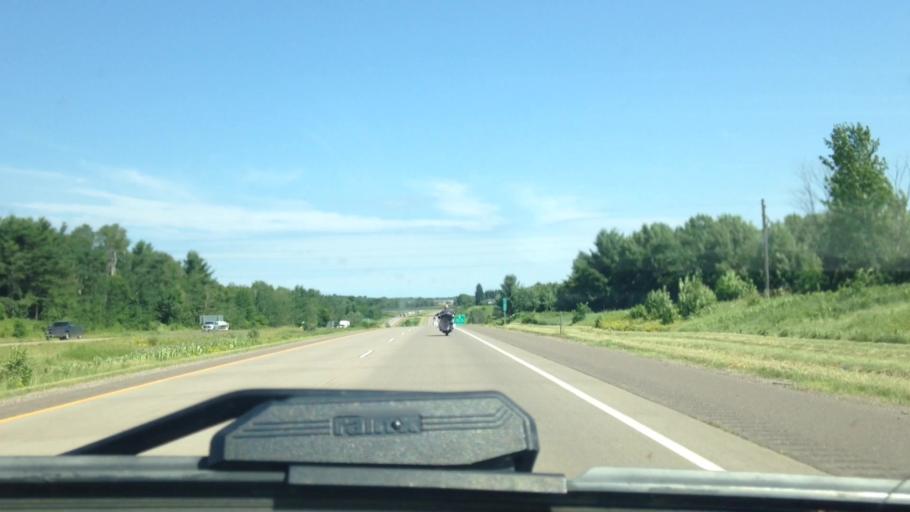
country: US
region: Wisconsin
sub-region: Barron County
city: Rice Lake
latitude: 45.4866
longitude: -91.7619
